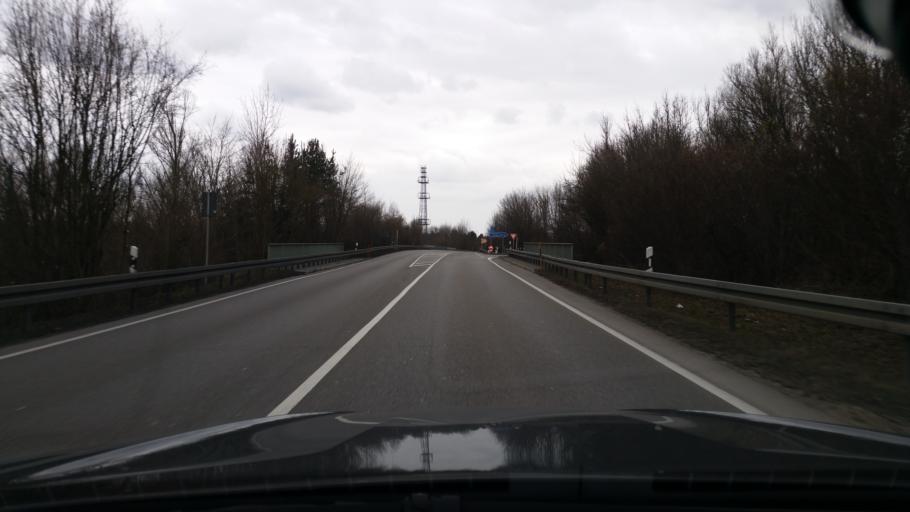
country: DE
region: Bavaria
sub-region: Upper Bavaria
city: Langenbach
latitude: 48.3947
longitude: 11.8579
